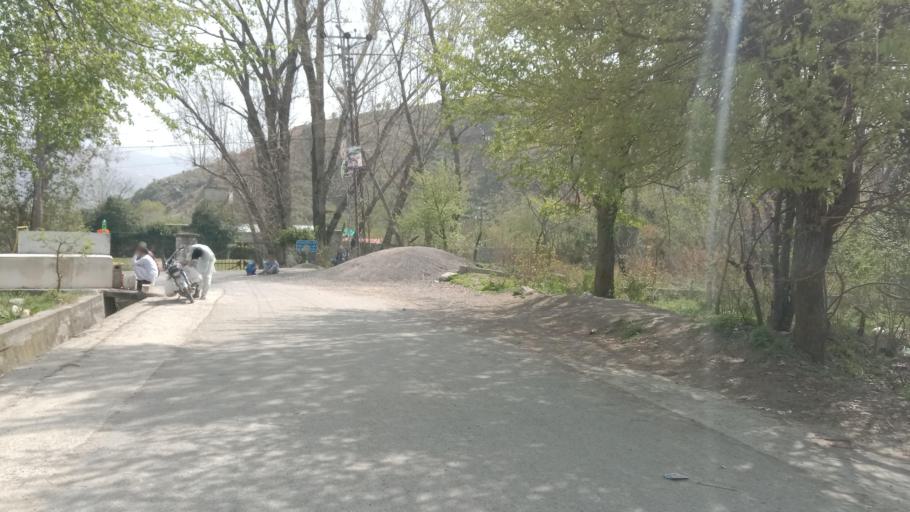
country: PK
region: Khyber Pakhtunkhwa
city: Abbottabad
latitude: 34.1543
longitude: 73.2602
